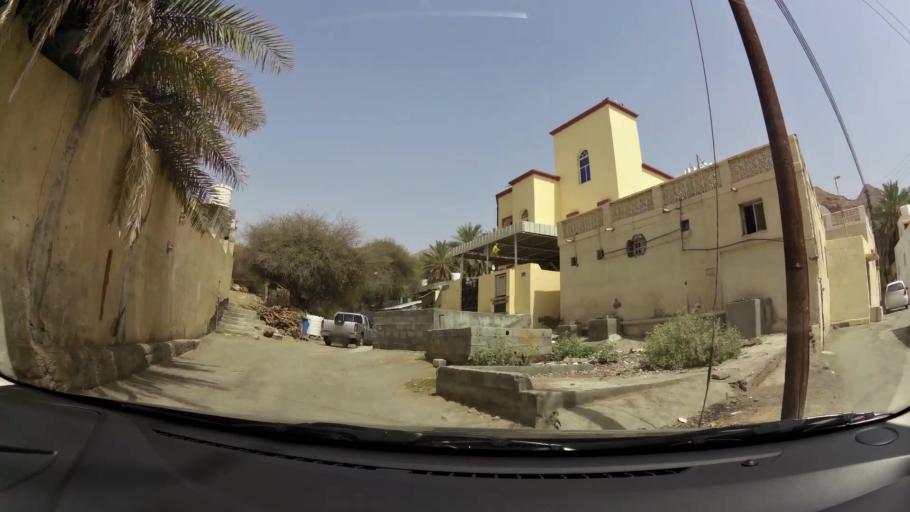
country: OM
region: Muhafazat Masqat
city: Bawshar
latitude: 23.5320
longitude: 58.3830
